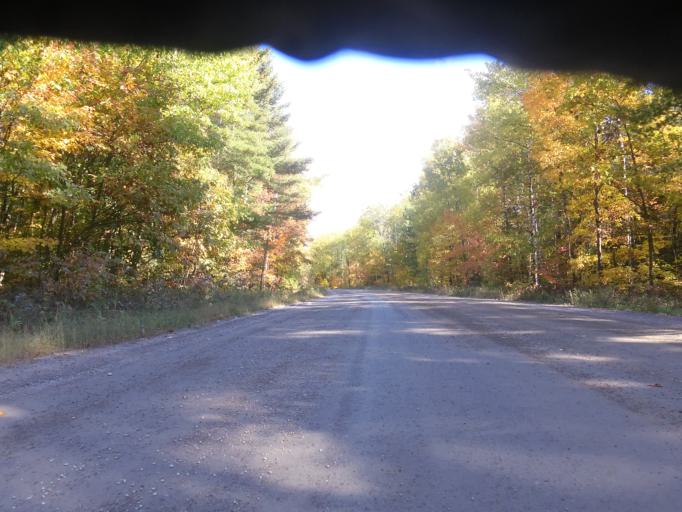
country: CA
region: Ontario
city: Petawawa
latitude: 45.8168
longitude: -77.4284
